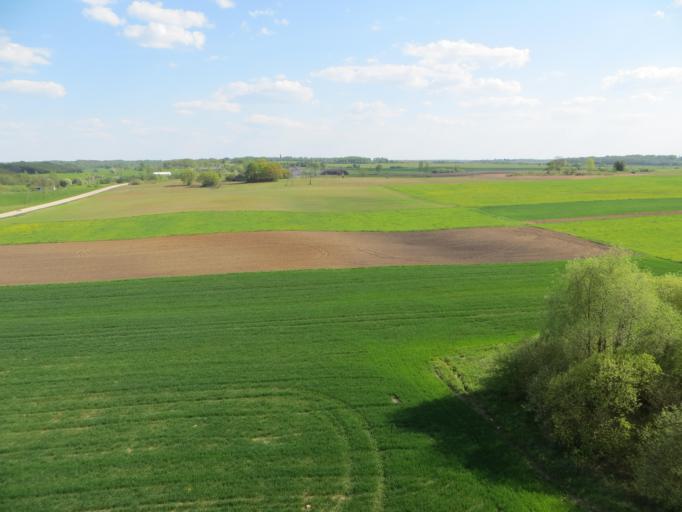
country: LT
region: Utenos apskritis
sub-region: Anyksciai
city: Anyksciai
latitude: 55.3716
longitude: 25.0341
